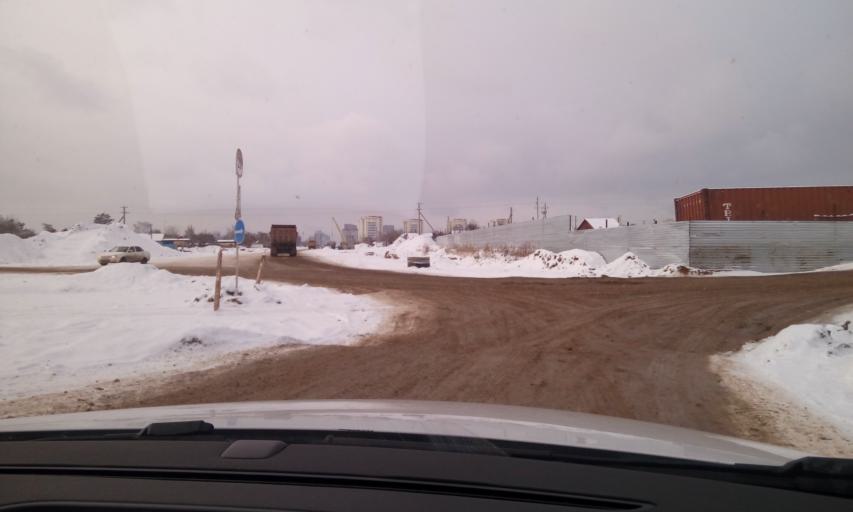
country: KZ
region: Astana Qalasy
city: Astana
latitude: 51.1173
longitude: 71.5167
